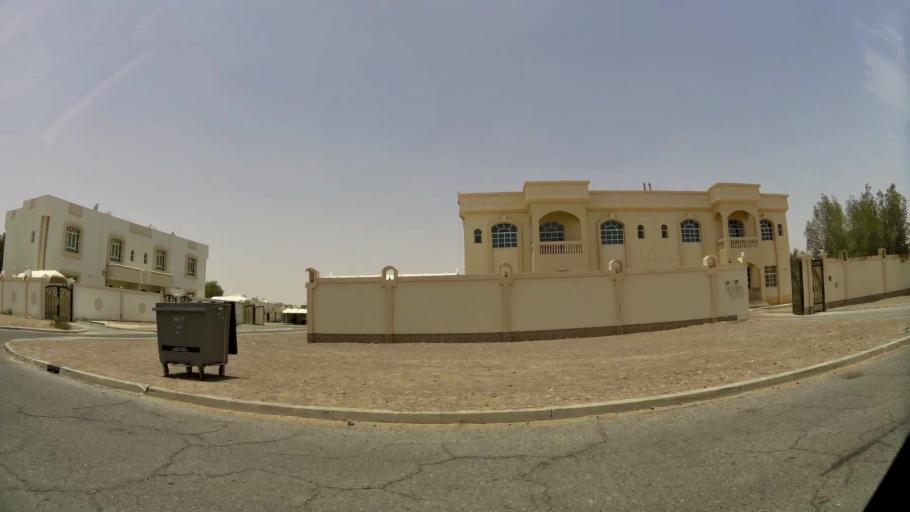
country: AE
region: Abu Dhabi
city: Al Ain
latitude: 24.2175
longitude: 55.7194
